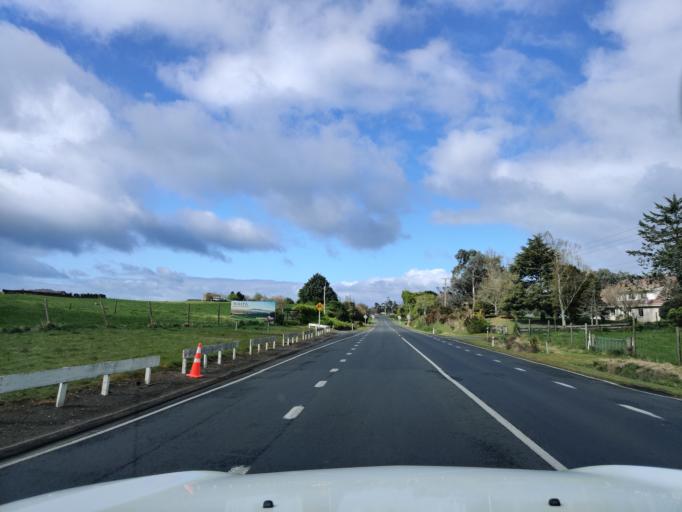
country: NZ
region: Waikato
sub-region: Hamilton City
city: Hamilton
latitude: -37.8325
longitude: 175.2179
